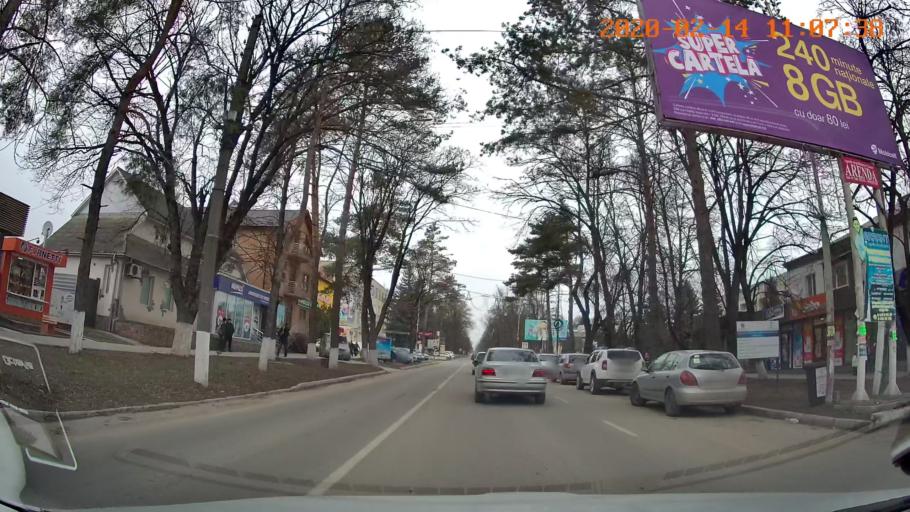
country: MD
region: Raionul Edinet
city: Edinet
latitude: 48.1699
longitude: 27.3054
